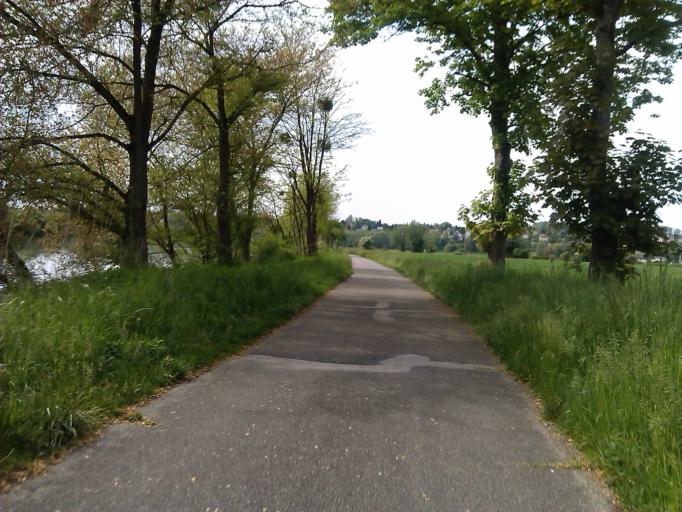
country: FR
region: Franche-Comte
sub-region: Departement du Doubs
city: Saint-Vit
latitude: 47.1707
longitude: 5.8099
